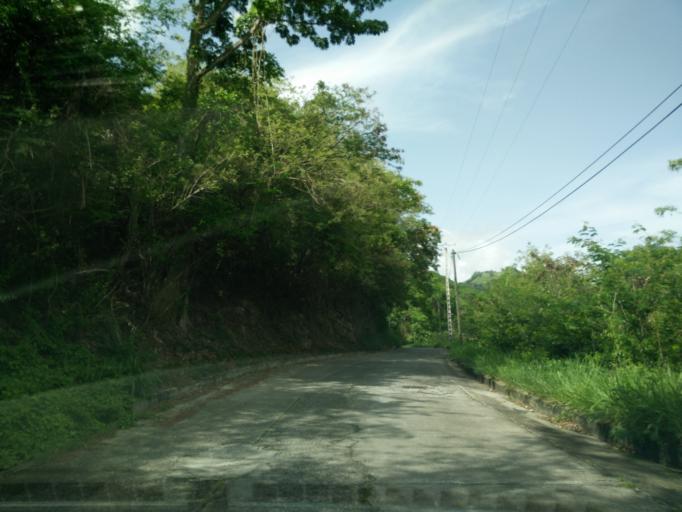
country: MQ
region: Martinique
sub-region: Martinique
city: Saint-Pierre
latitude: 14.7118
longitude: -61.1771
